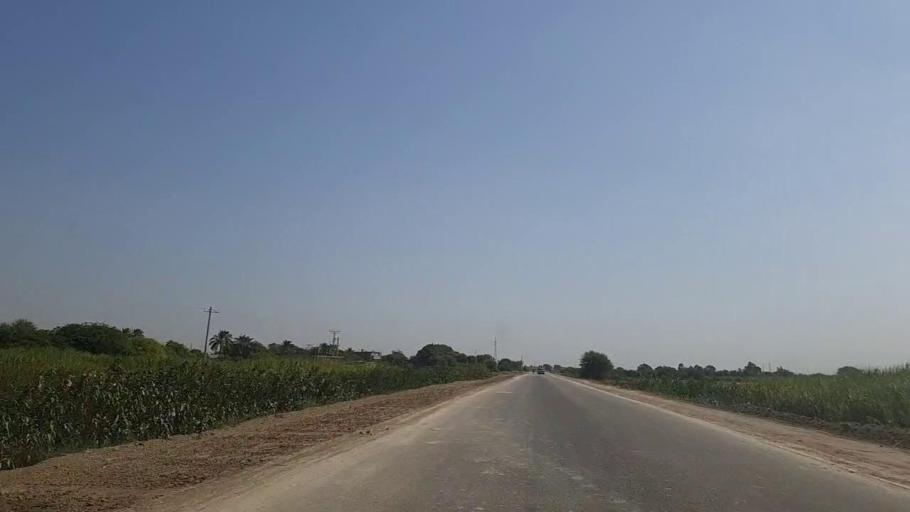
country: PK
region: Sindh
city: Mirpur Batoro
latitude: 24.7448
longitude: 68.2437
